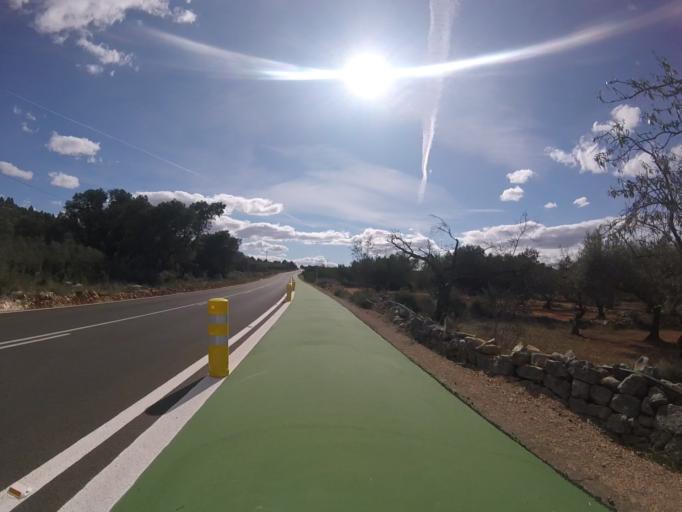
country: ES
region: Valencia
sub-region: Provincia de Castello
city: Cati
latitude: 40.4148
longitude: 0.0710
